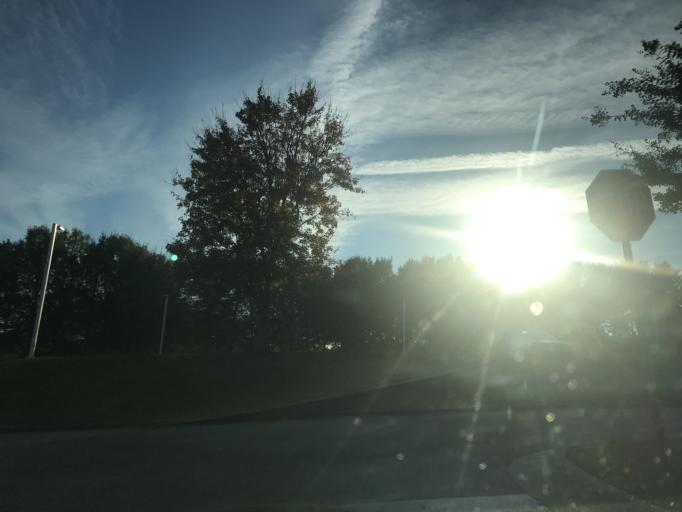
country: US
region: North Carolina
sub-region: Wake County
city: Wake Forest
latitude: 35.9083
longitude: -78.5990
